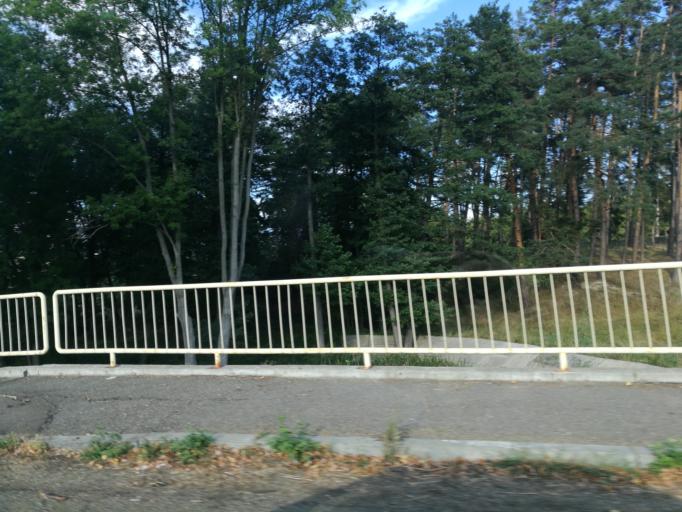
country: RO
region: Suceava
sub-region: Comuna Mitocu Dragomirnei
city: Mitocu Dragomirnei
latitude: 47.7556
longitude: 26.2284
